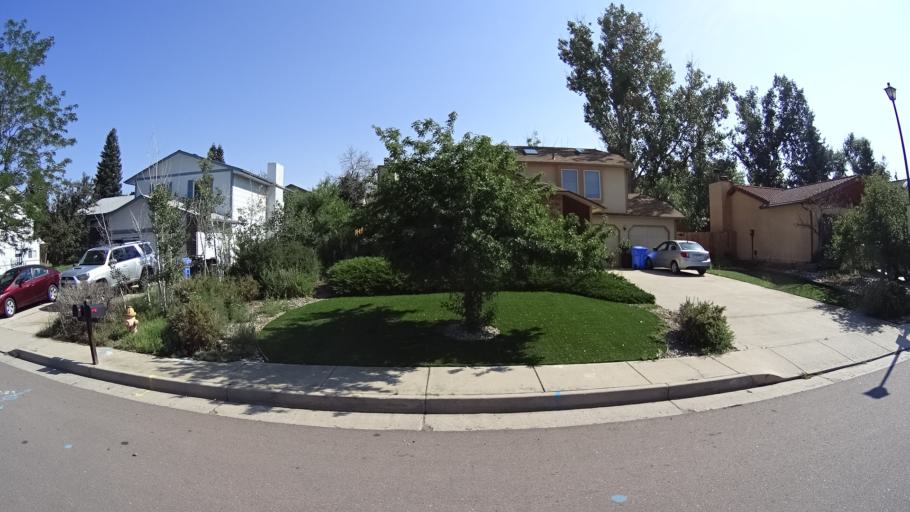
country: US
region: Colorado
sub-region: El Paso County
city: Air Force Academy
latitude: 38.9564
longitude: -104.7821
